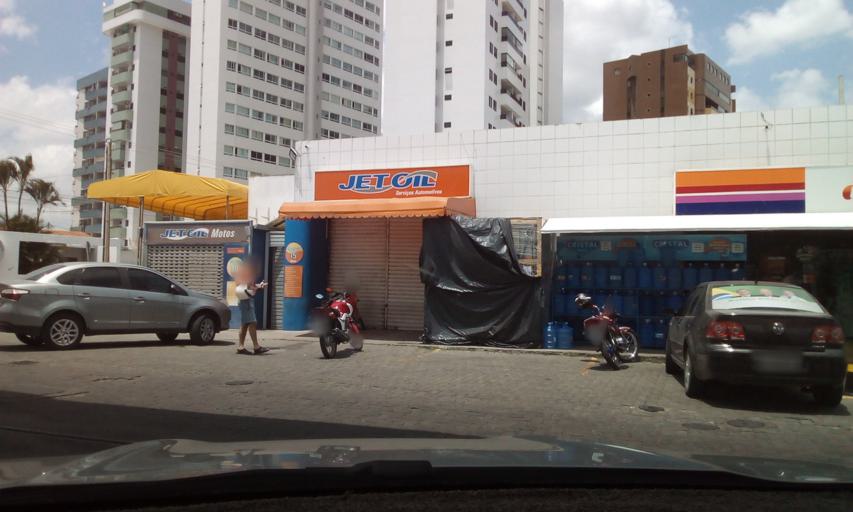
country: BR
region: Pernambuco
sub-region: Caruaru
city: Caruaru
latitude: -8.2688
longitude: -35.9761
